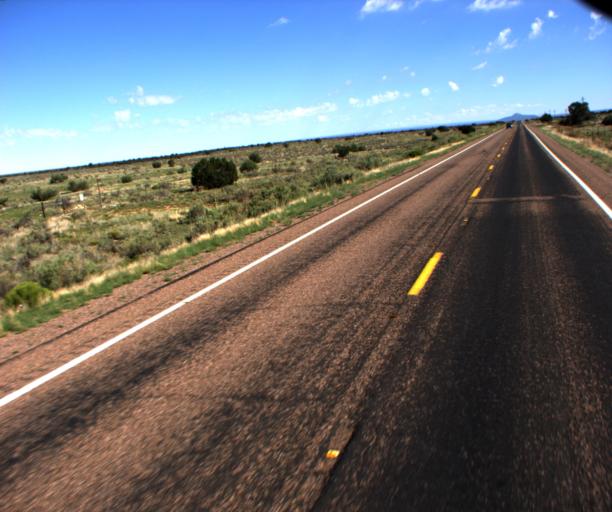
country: US
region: Arizona
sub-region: Coconino County
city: Williams
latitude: 35.5795
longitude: -112.1527
